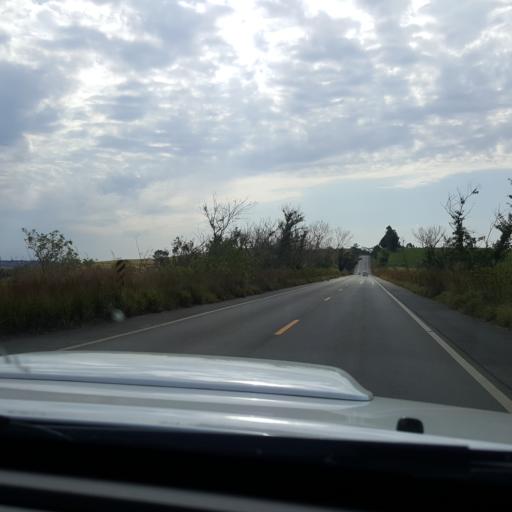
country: BR
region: Sao Paulo
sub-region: Itaporanga
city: Itaporanga
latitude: -23.7561
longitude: -49.4509
